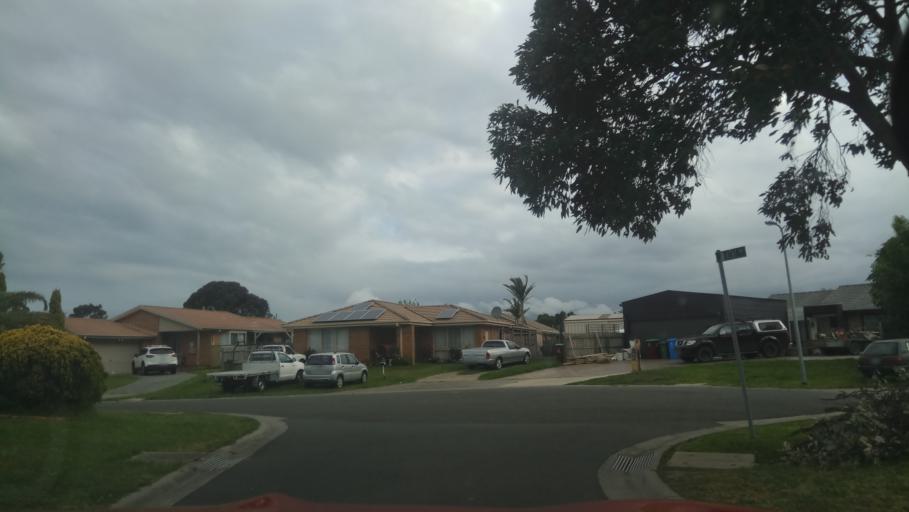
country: AU
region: Victoria
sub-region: Casey
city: Lynbrook
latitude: -38.0703
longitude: 145.2645
